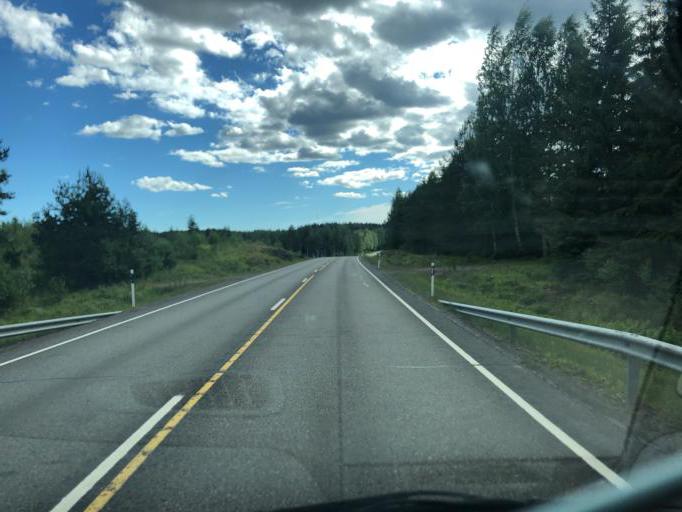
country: FI
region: Kymenlaakso
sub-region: Kouvola
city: Kouvola
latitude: 61.0042
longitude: 26.9433
